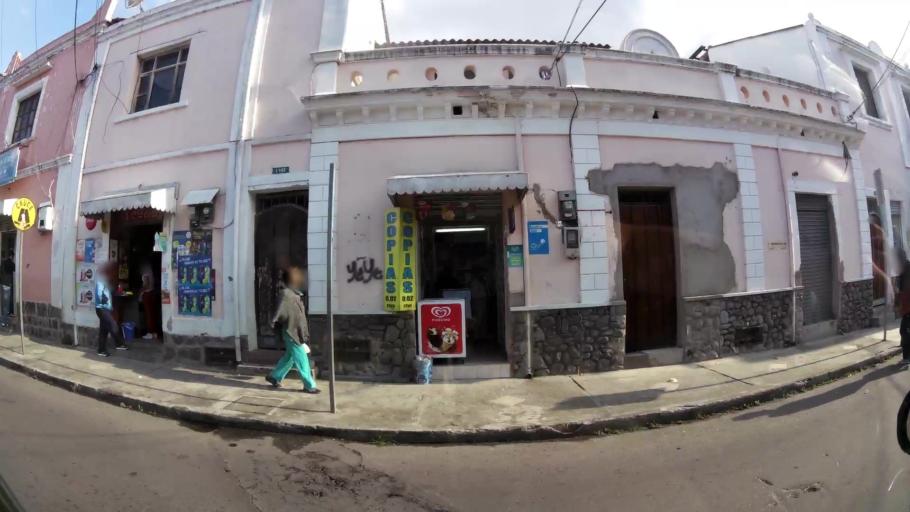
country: EC
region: Pichincha
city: Sangolqui
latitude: -0.2919
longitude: -78.4768
